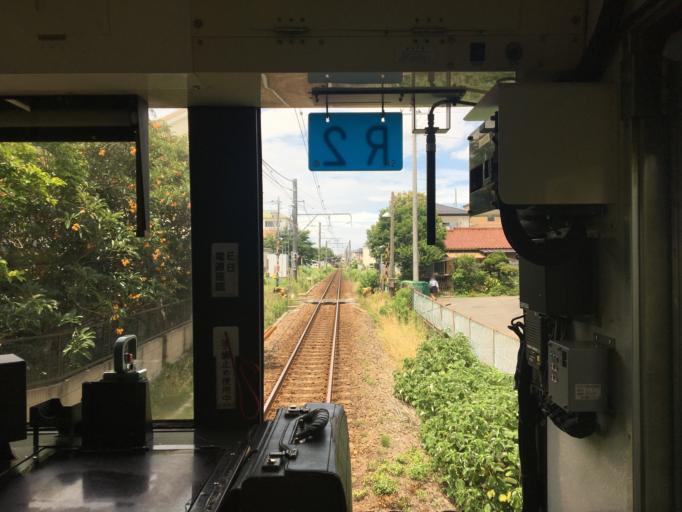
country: JP
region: Kanagawa
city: Chigasaki
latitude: 35.3540
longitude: 139.4004
